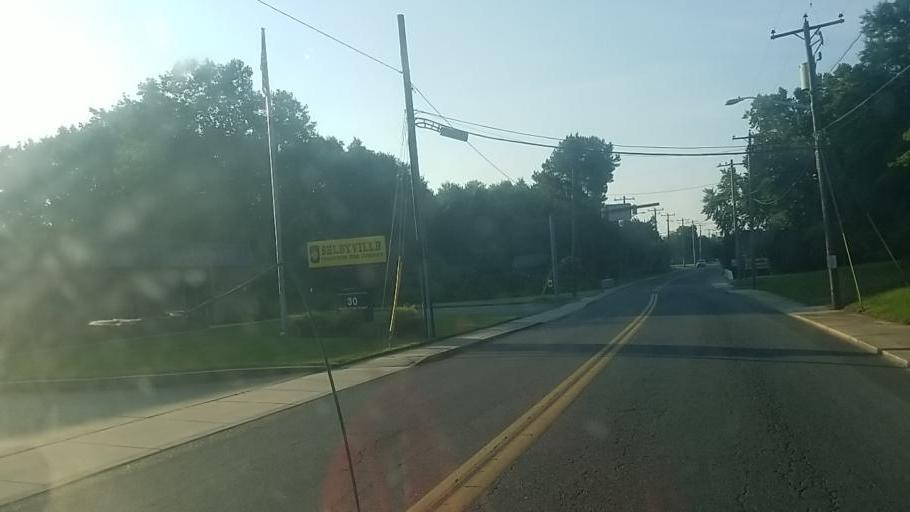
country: US
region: Delaware
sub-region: Sussex County
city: Selbyville
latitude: 38.4632
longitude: -75.2234
